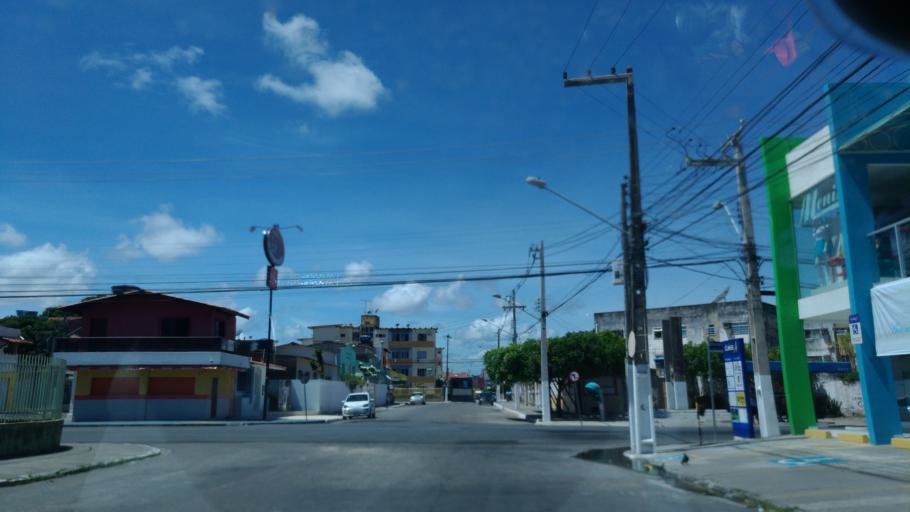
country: BR
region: Alagoas
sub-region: Maceio
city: Maceio
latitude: -9.6573
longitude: -35.7115
